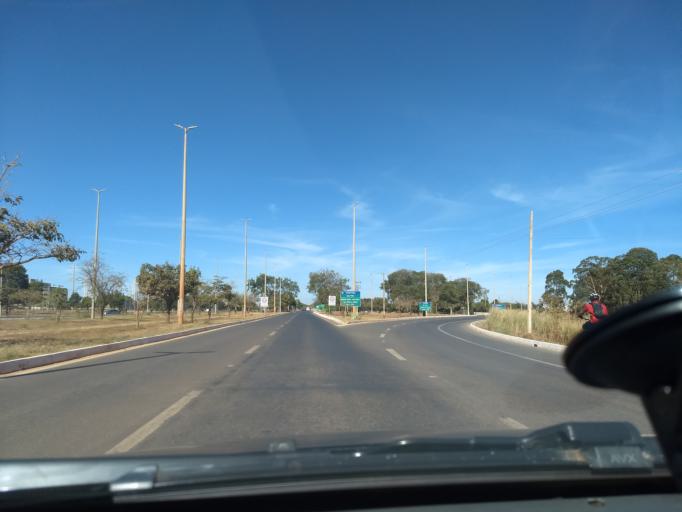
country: BR
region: Federal District
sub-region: Brasilia
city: Brasilia
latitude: -15.7901
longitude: -48.0527
